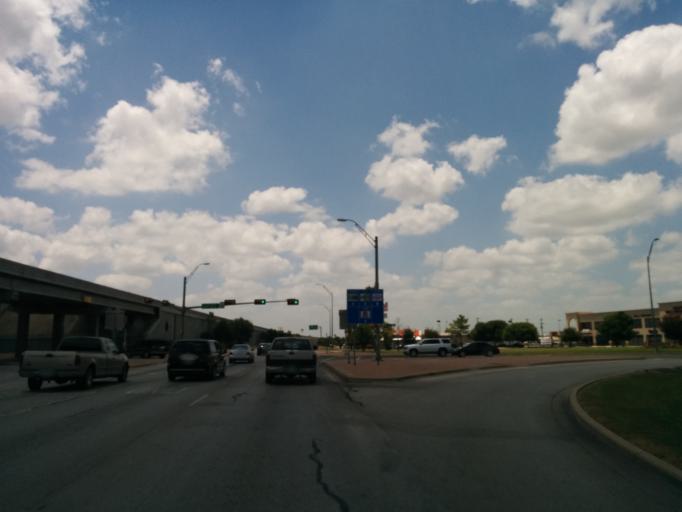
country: US
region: Texas
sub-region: Bastrop County
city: Bastrop
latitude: 30.1054
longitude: -97.3284
